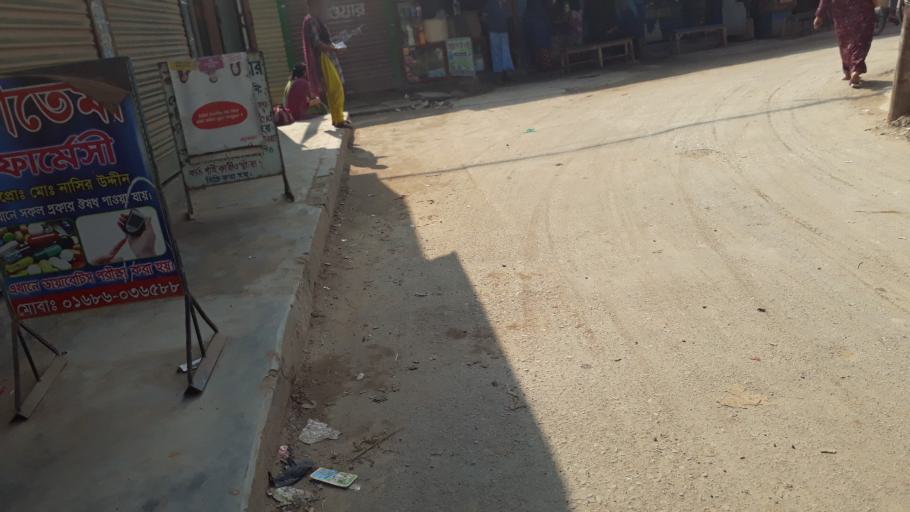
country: BD
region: Dhaka
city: Tungi
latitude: 23.8509
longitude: 90.2517
